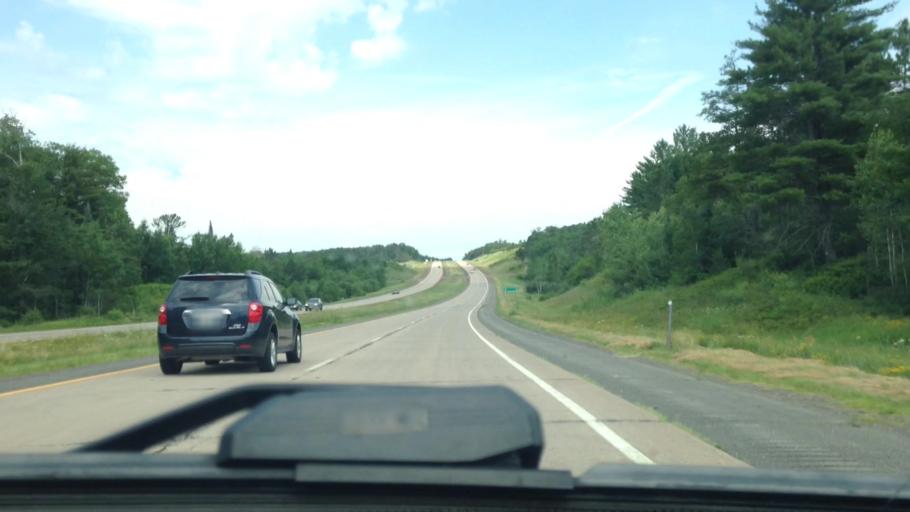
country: US
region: Wisconsin
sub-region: Douglas County
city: Lake Nebagamon
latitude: 46.3242
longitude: -91.8171
